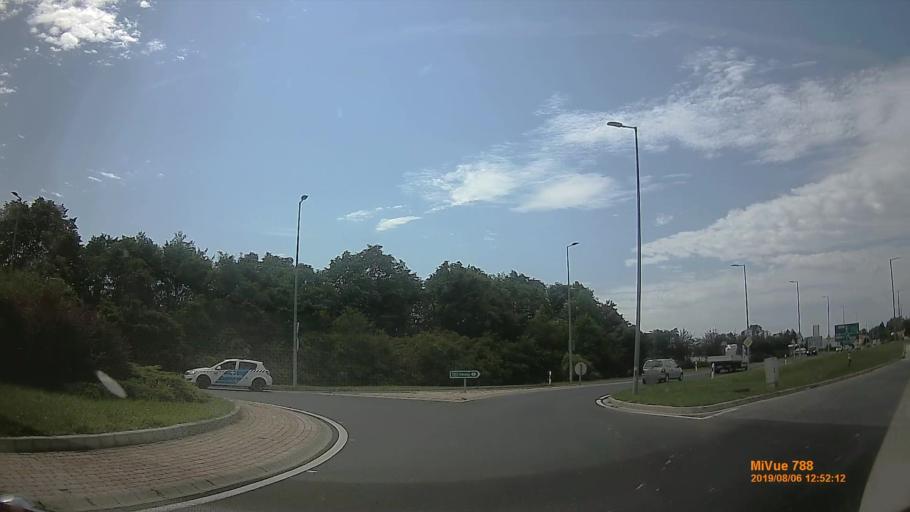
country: HU
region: Vas
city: Szombathely
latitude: 47.2548
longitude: 16.6199
